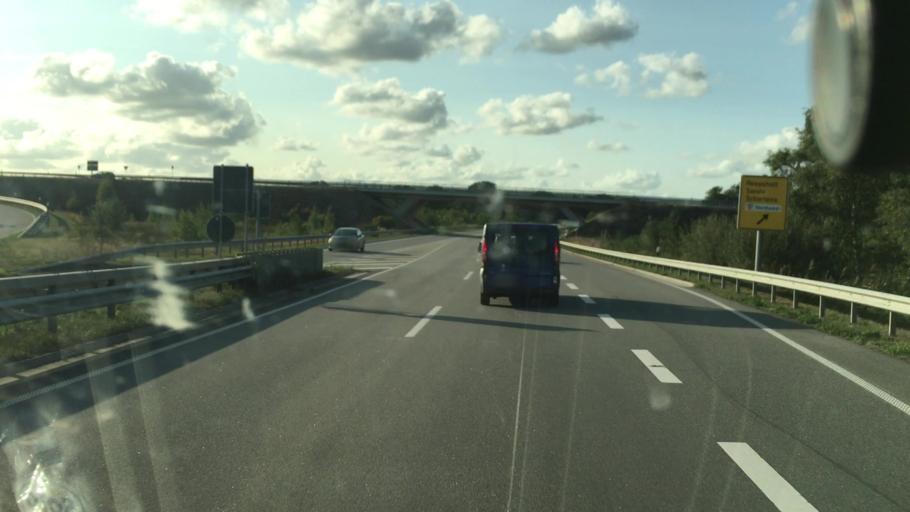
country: DE
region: Lower Saxony
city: Schortens
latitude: 53.5420
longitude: 7.9719
